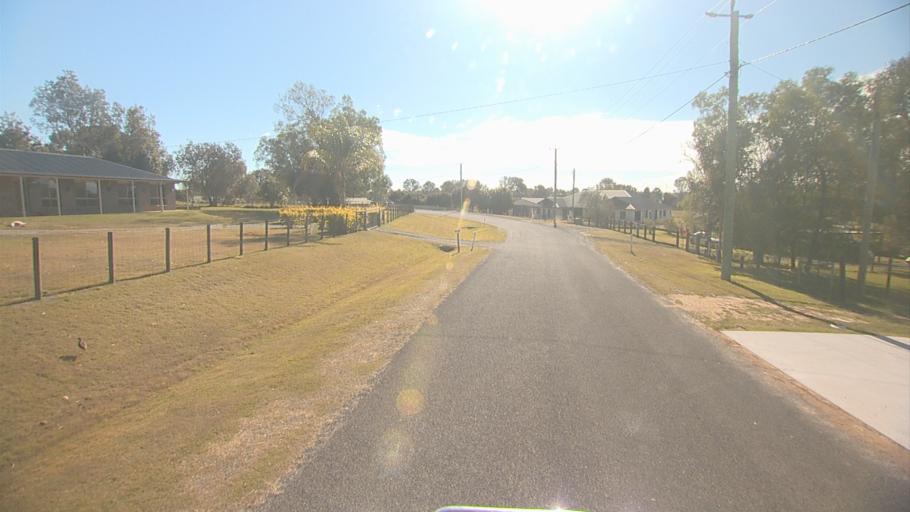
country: AU
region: Queensland
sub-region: Logan
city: Chambers Flat
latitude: -27.7731
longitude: 153.0808
